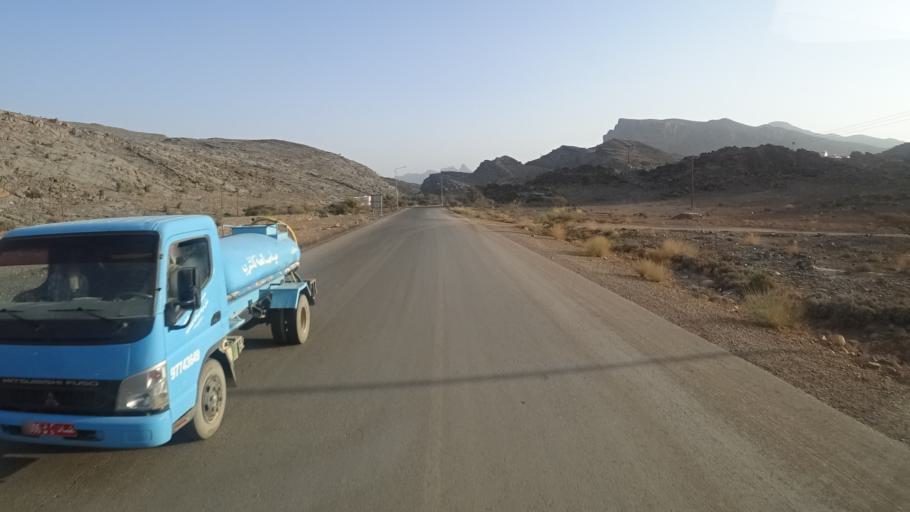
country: OM
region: Muhafazat ad Dakhiliyah
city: Bahla'
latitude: 23.2406
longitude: 57.1499
